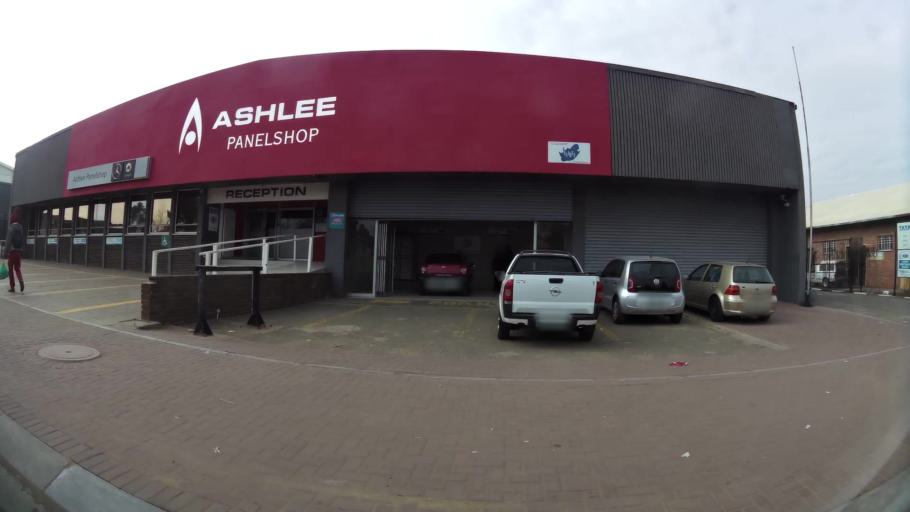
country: ZA
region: Orange Free State
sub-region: Mangaung Metropolitan Municipality
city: Bloemfontein
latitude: -29.1303
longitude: 26.2228
